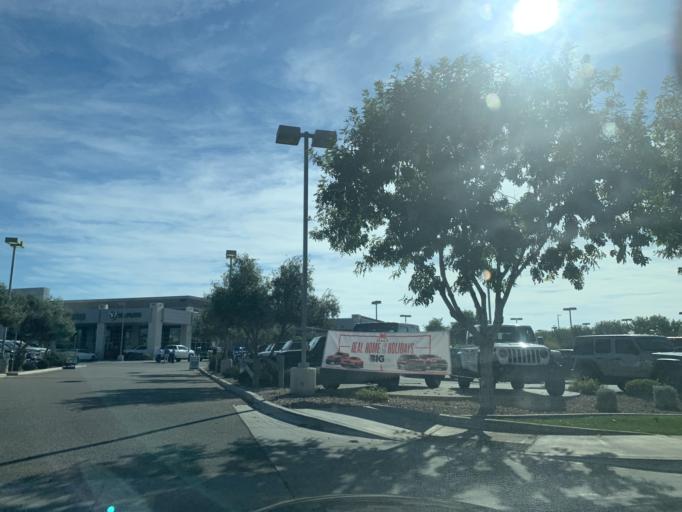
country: US
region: Arizona
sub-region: Maricopa County
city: Gilbert
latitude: 33.2918
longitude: -111.7573
